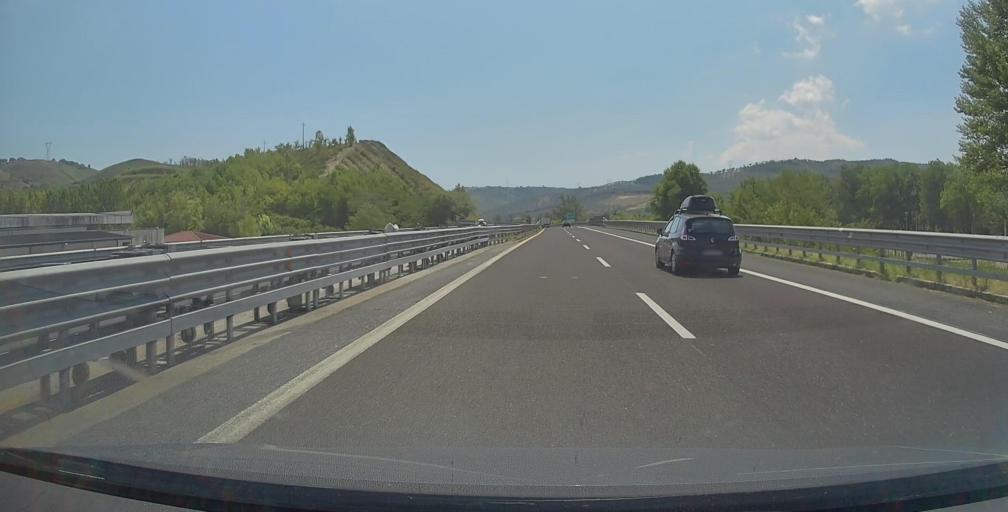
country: IT
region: Calabria
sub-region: Provincia di Vibo-Valentia
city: Soriano Calabro
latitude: 38.6326
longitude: 16.1691
